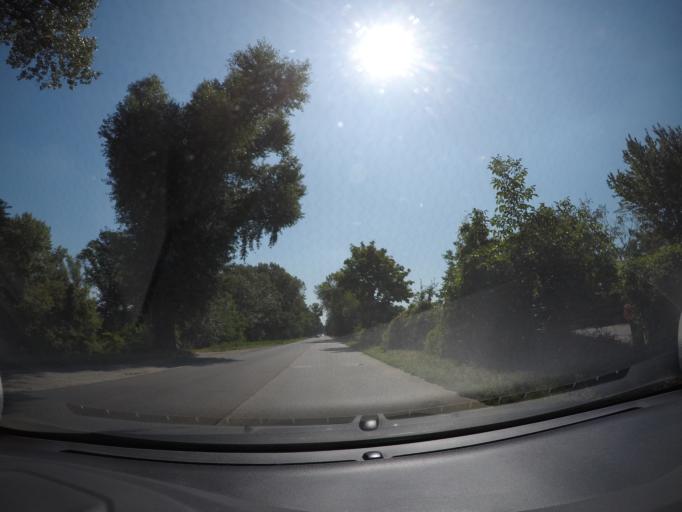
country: AT
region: Lower Austria
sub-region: Politischer Bezirk Wien-Umgebung
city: Schwechat
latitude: 48.2016
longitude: 16.4550
